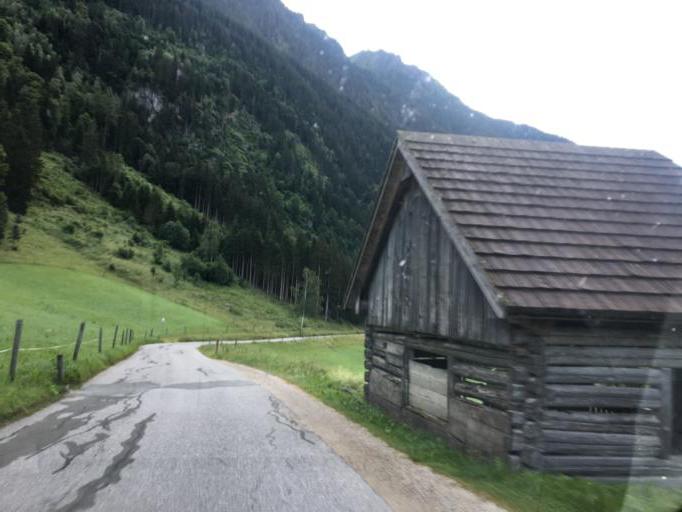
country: AT
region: Styria
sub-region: Politischer Bezirk Liezen
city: Schladming
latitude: 47.3554
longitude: 13.7155
